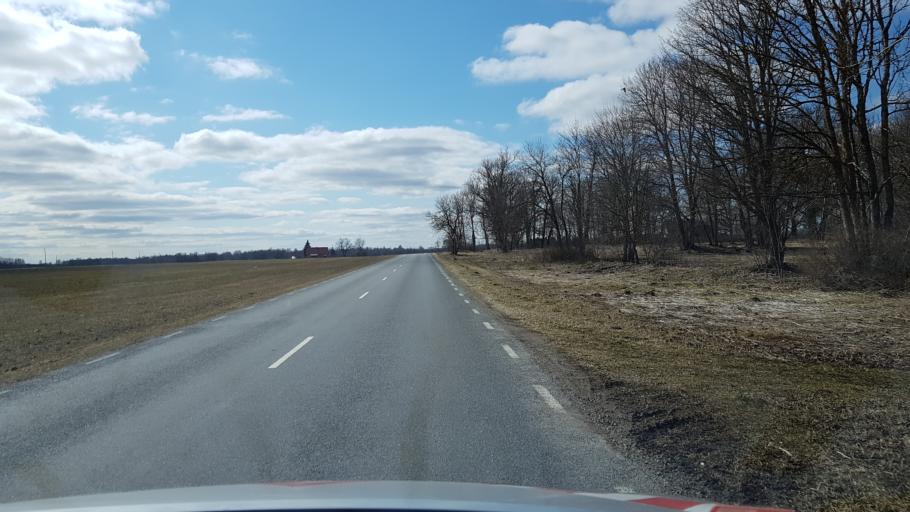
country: EE
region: Laeaene-Virumaa
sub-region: Tapa vald
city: Tapa
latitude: 59.2722
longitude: 25.8632
